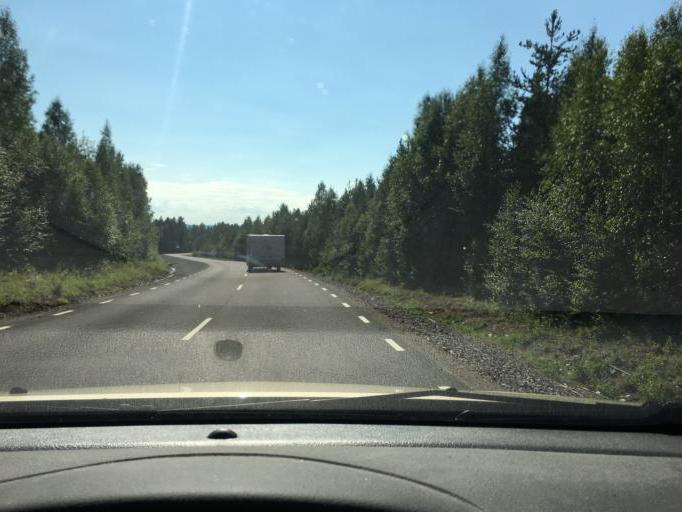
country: SE
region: Norrbotten
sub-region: Lulea Kommun
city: Ranea
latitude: 66.0497
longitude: 22.2088
